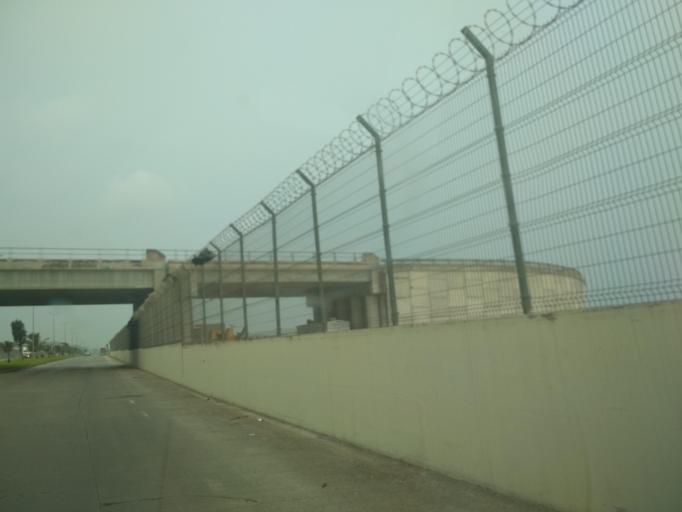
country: MX
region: Veracruz
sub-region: Veracruz
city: Rio Medio [Granja]
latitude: 19.2273
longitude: -96.1925
